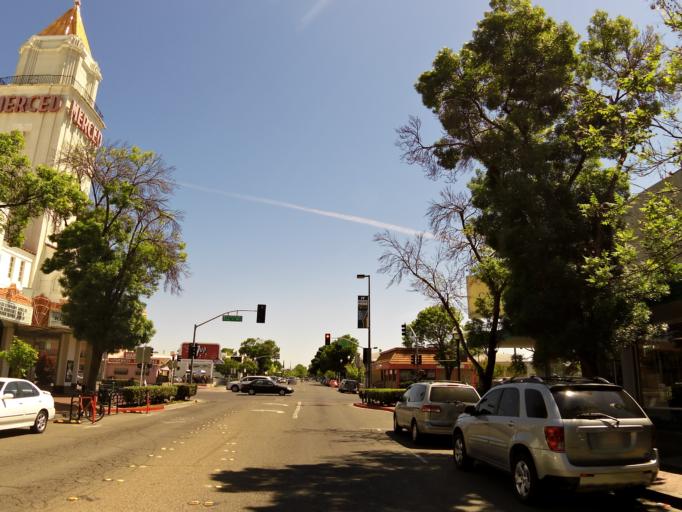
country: US
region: California
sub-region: Merced County
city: Merced
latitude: 37.3005
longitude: -120.4809
